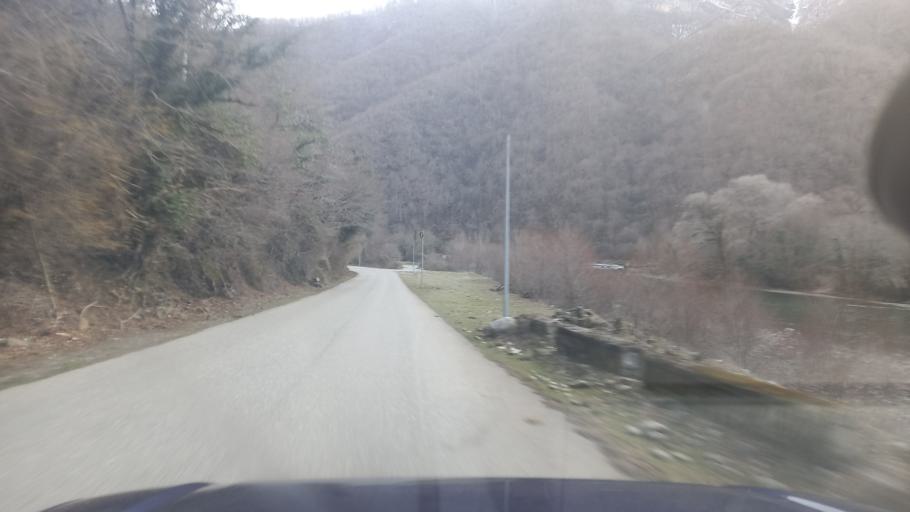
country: GE
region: Abkhazia
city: Gagra
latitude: 43.3074
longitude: 40.4079
